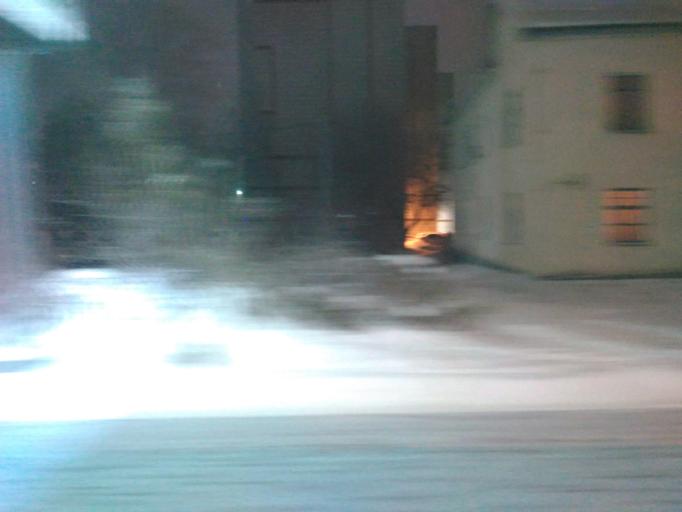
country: RU
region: Ulyanovsk
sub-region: Ulyanovskiy Rayon
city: Ulyanovsk
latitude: 54.3243
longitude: 48.3816
